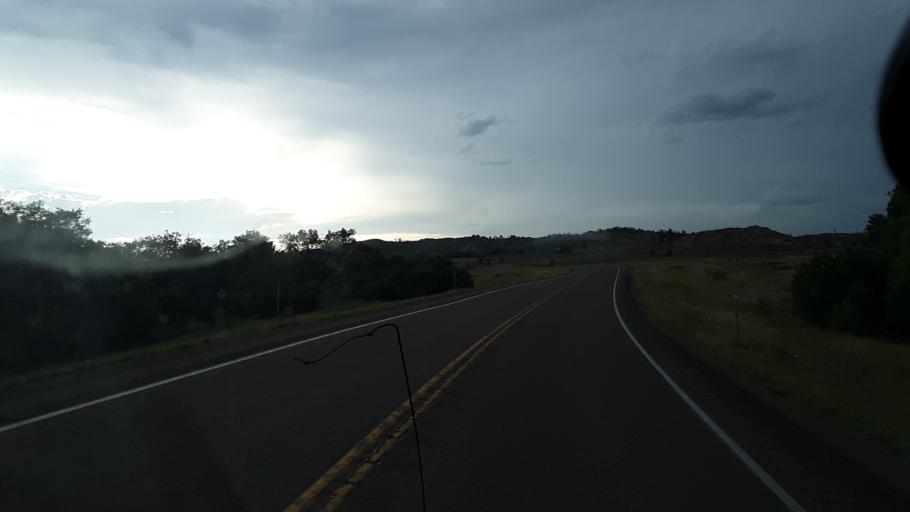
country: US
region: Montana
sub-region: Rosebud County
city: Lame Deer
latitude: 45.6193
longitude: -106.4100
